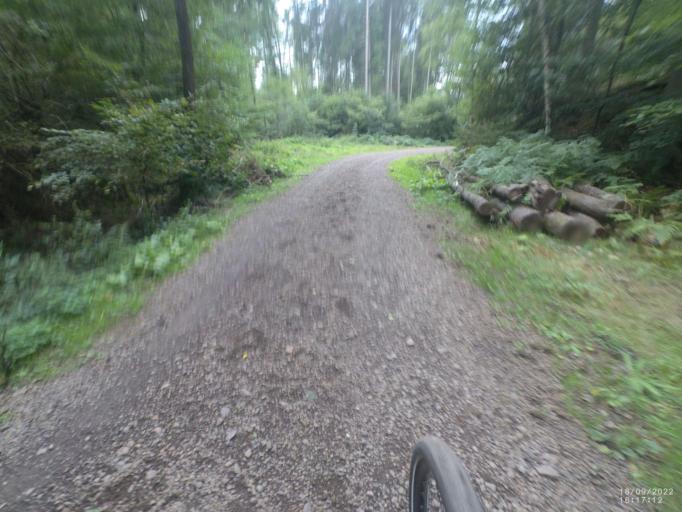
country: DE
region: Rheinland-Pfalz
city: Deudesfeld
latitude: 50.1064
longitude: 6.7177
